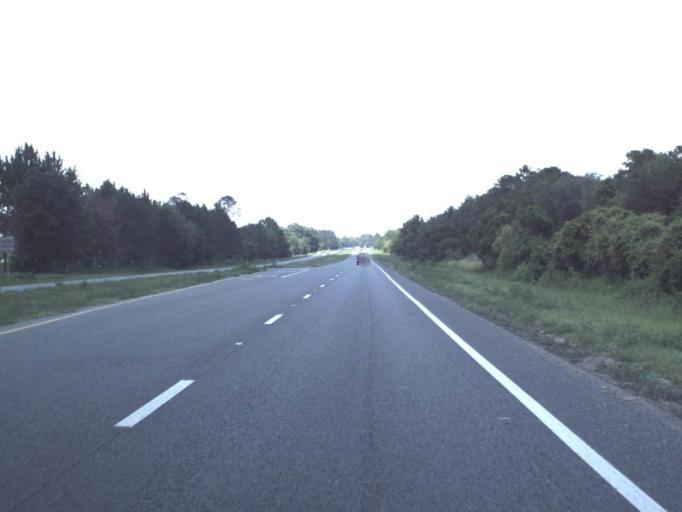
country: US
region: Florida
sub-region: Putnam County
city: East Palatka
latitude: 29.7550
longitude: -81.6408
